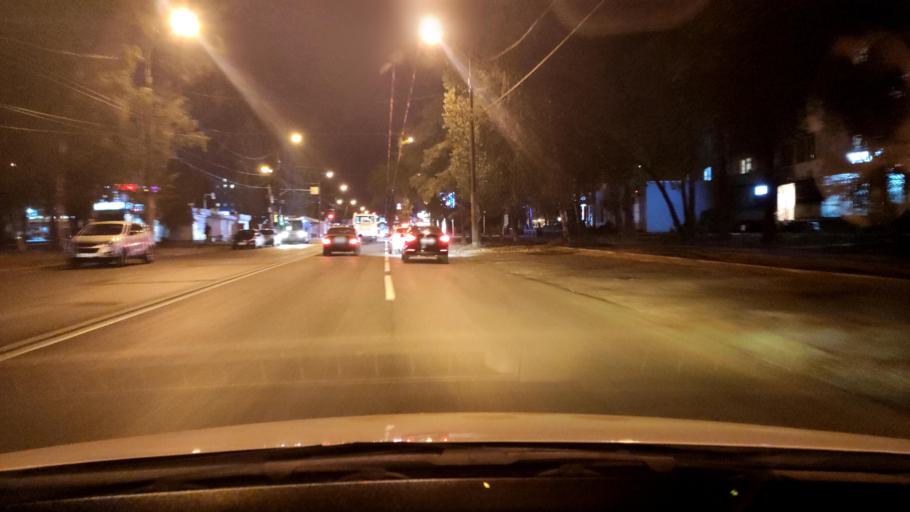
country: RU
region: Voronezj
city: Voronezh
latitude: 51.7056
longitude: 39.1743
